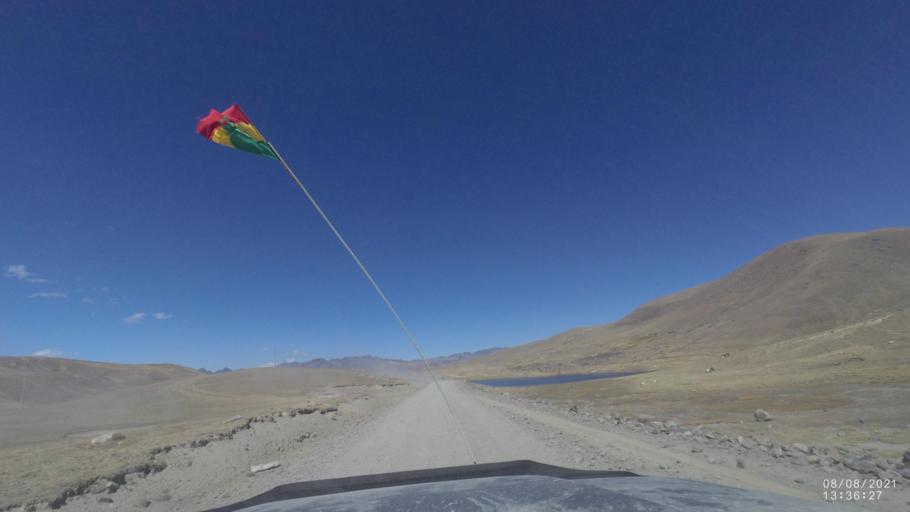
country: BO
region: Cochabamba
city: Colchani
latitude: -17.0731
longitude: -66.5026
